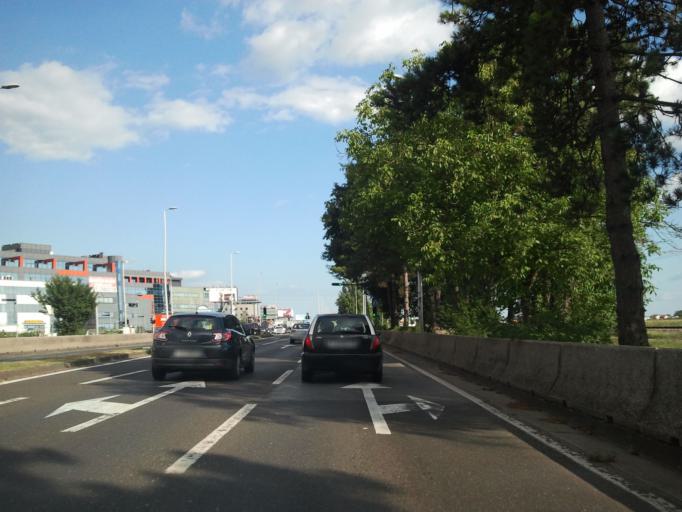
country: HR
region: Grad Zagreb
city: Odra
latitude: 45.7485
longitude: 15.9918
